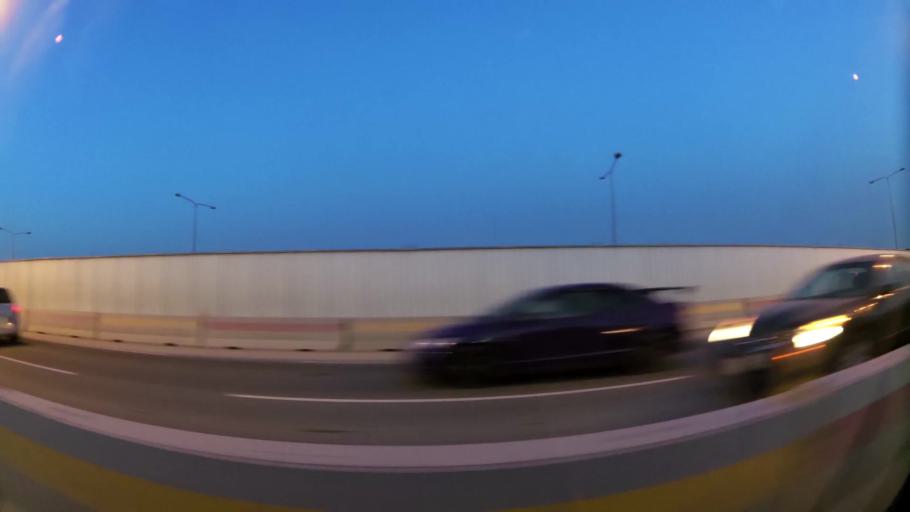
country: QA
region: Baladiyat ar Rayyan
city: Ar Rayyan
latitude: 25.3081
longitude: 51.4542
